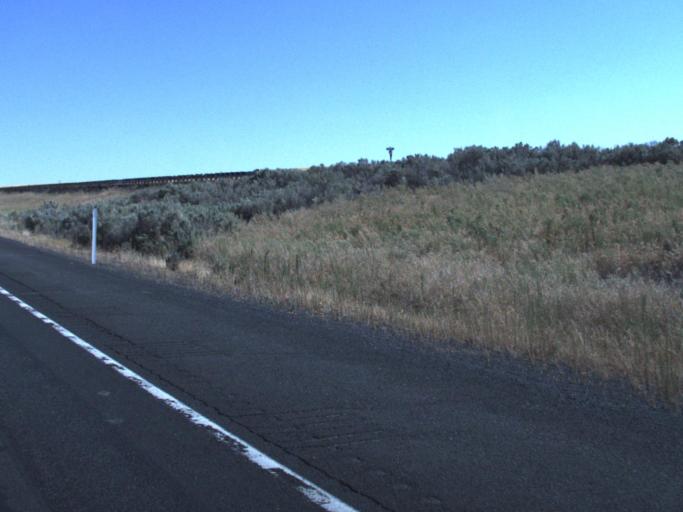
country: US
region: Washington
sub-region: Adams County
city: Ritzville
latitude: 47.1103
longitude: -118.5497
